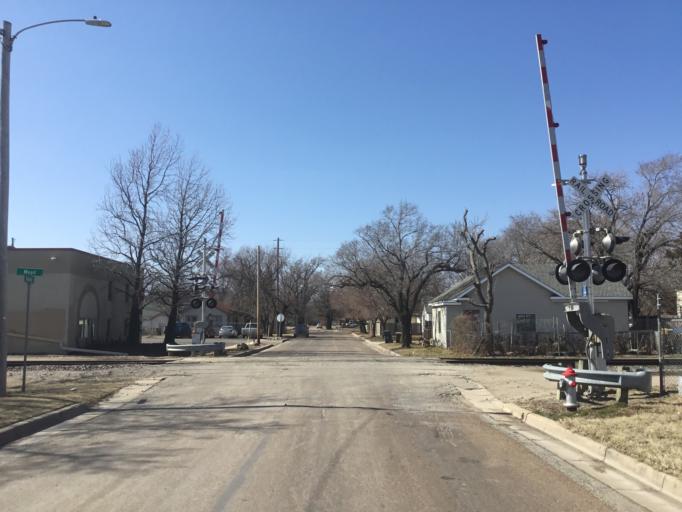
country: US
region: Kansas
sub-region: Sedgwick County
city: Wichita
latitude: 37.6699
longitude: -97.3287
